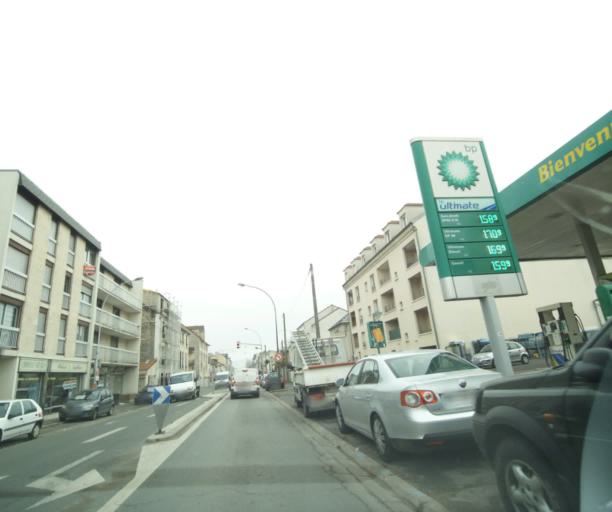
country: FR
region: Ile-de-France
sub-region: Departement de Seine-Saint-Denis
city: Vaujours
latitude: 48.9348
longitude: 2.5675
